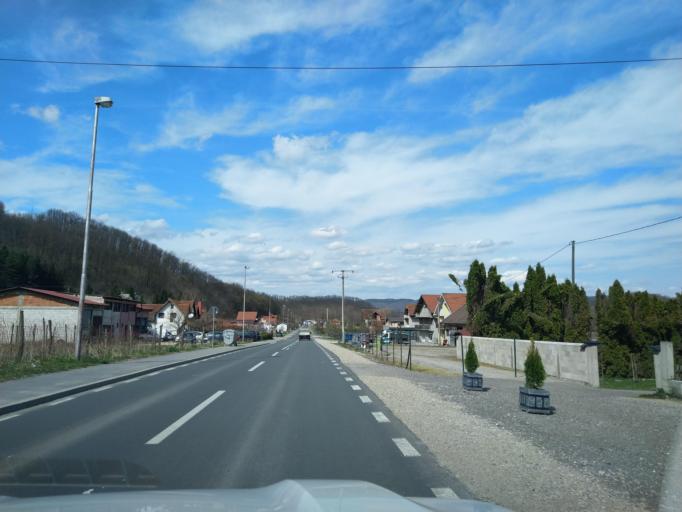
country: RS
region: Central Serbia
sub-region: Zlatiborski Okrug
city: Arilje
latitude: 43.7718
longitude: 20.1005
